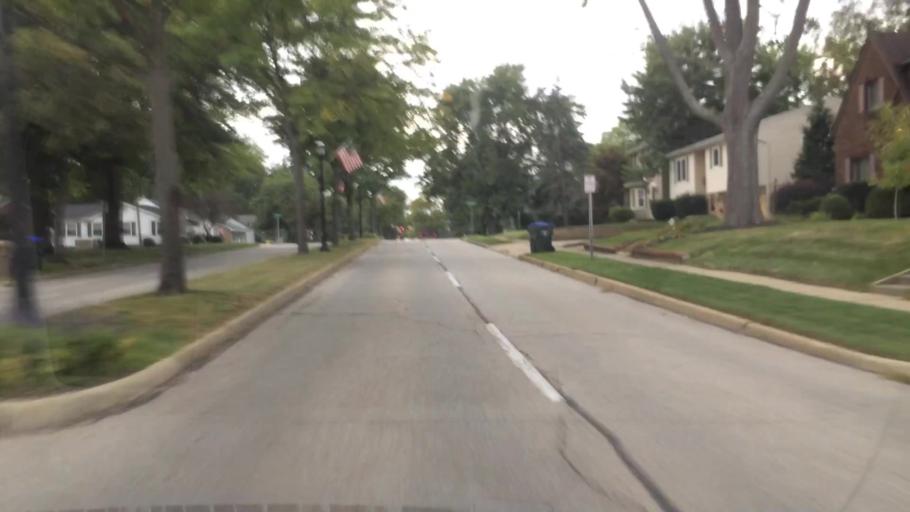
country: US
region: Ohio
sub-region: Summit County
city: Cuyahoga Falls
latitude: 41.1345
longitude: -81.5041
